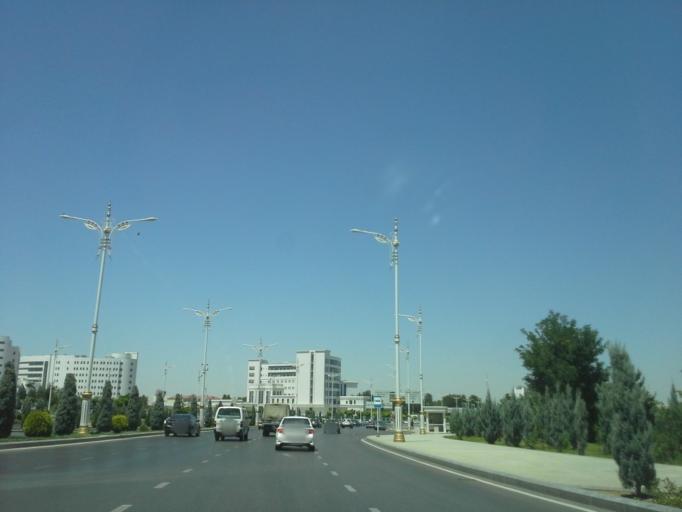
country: TM
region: Ahal
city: Ashgabat
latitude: 37.9376
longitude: 58.3651
